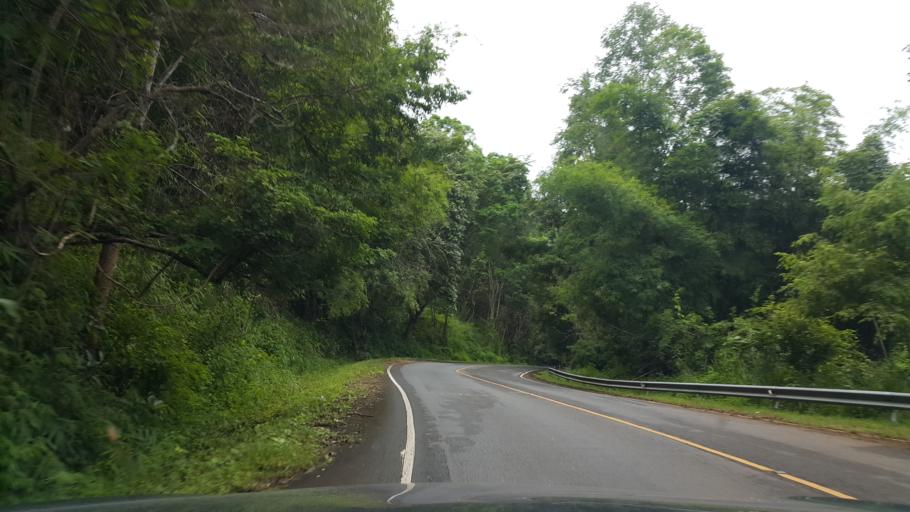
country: TH
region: Chiang Mai
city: Samoeng
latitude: 18.8228
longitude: 98.7861
